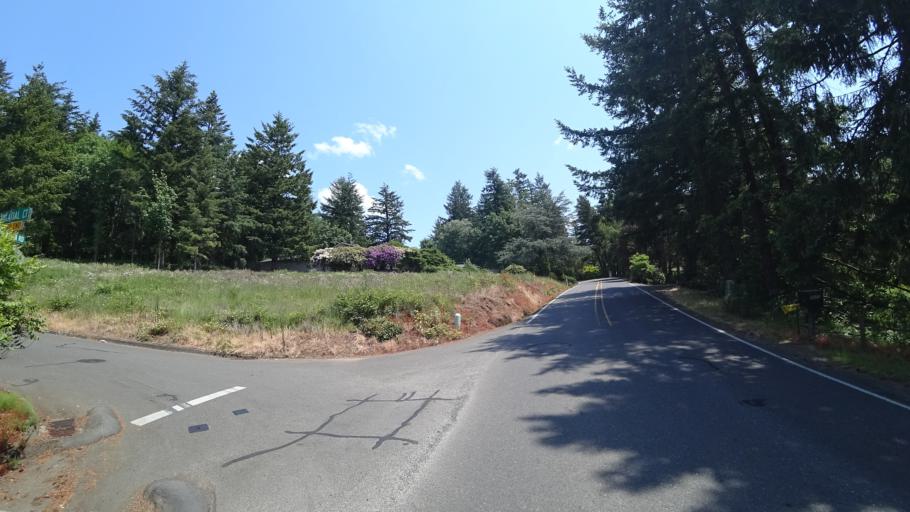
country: US
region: Oregon
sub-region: Clackamas County
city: Happy Valley
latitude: 45.4489
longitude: -122.5539
